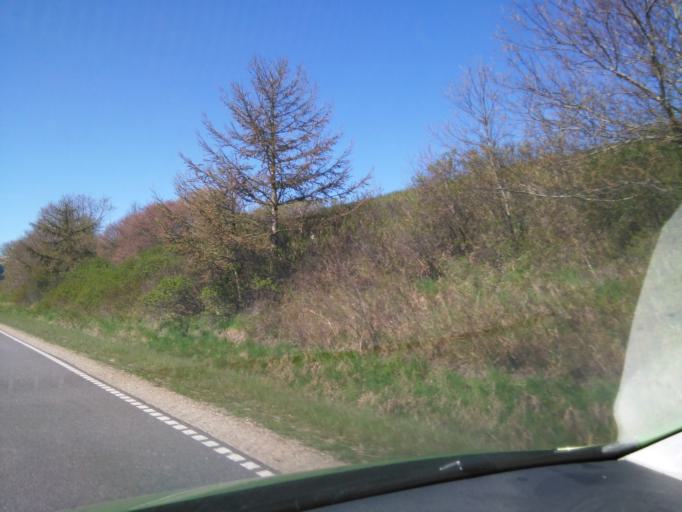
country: DK
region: South Denmark
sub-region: Varde Kommune
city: Oksbol
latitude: 55.6193
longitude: 8.2991
